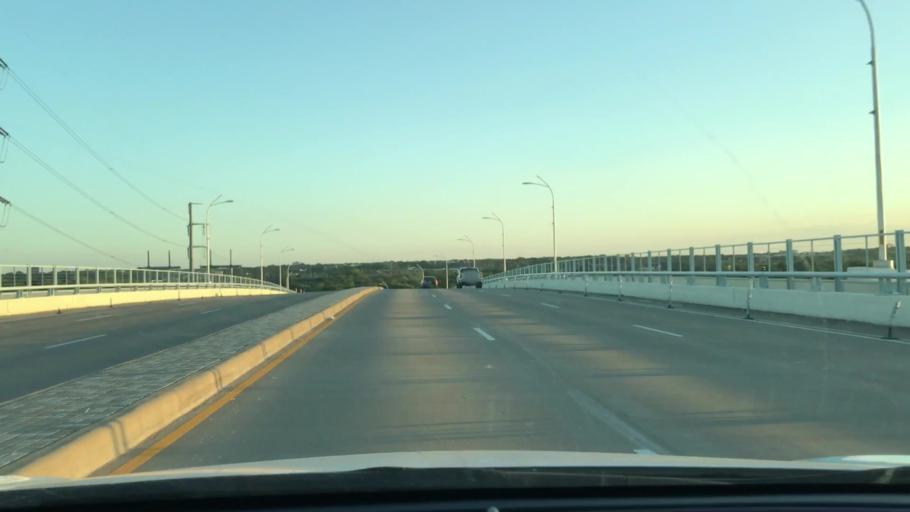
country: US
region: Texas
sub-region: Dallas County
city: Dallas
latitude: 32.7876
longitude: -96.8357
